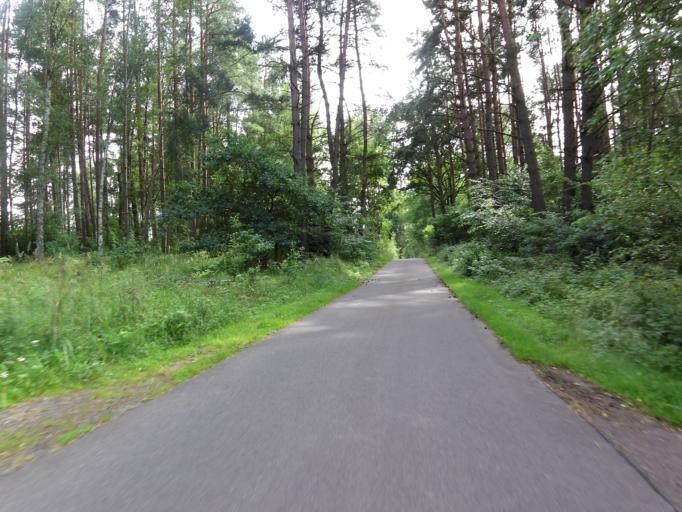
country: DE
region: Brandenburg
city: Lychen
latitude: 53.2344
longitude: 13.2845
